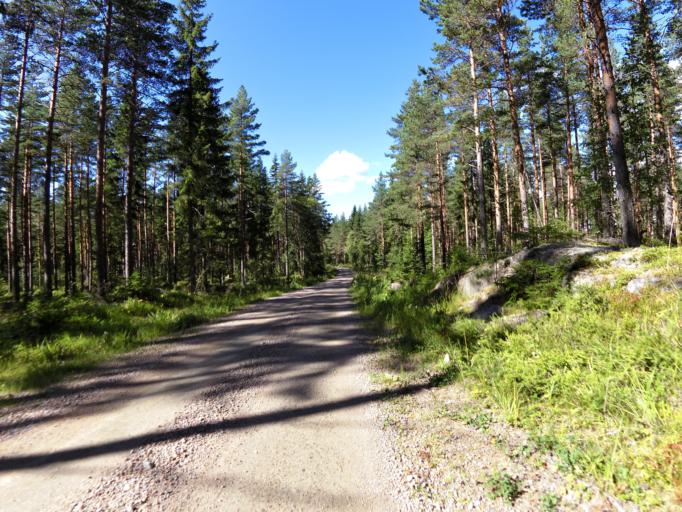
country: SE
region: Gaevleborg
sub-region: Gavle Kommun
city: Valbo
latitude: 60.7868
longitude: 16.8965
